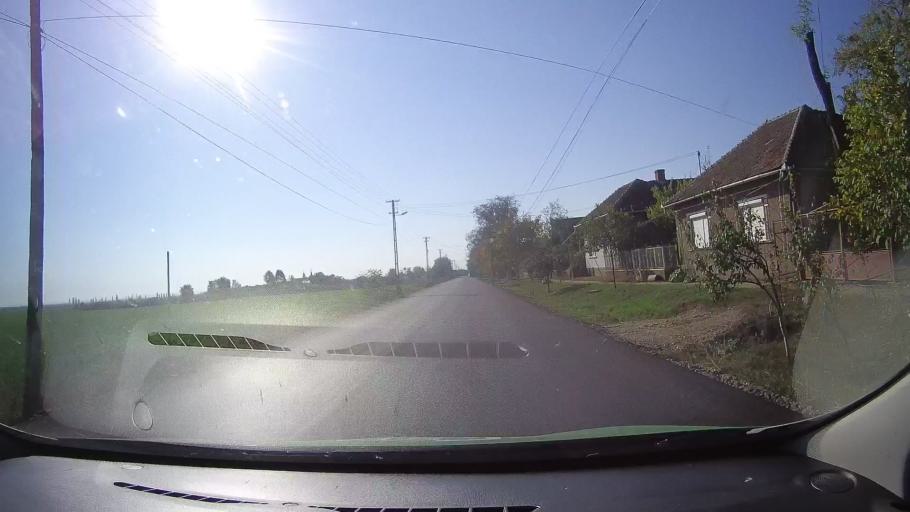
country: RO
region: Satu Mare
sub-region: Comuna Tiream
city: Tiream
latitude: 47.6219
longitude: 22.4681
